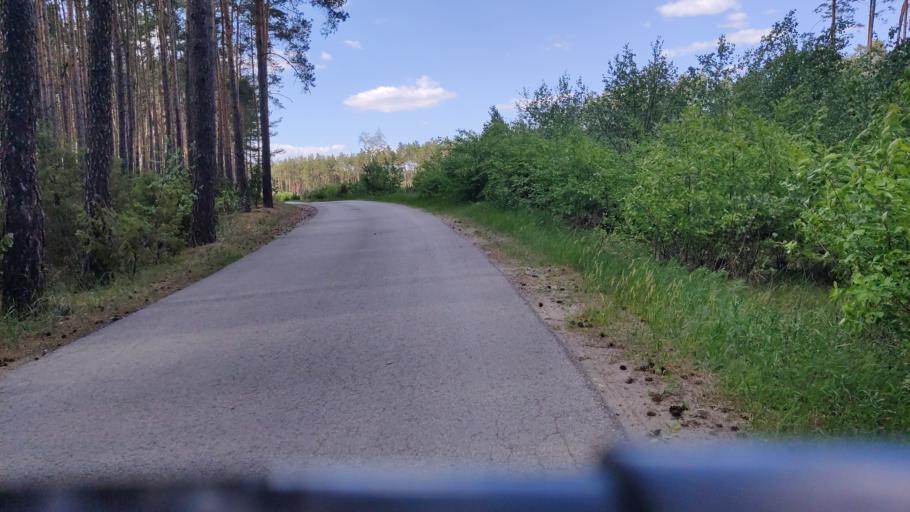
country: PL
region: Kujawsko-Pomorskie
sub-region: Wloclawek
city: Wloclawek
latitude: 52.5977
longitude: 19.0832
